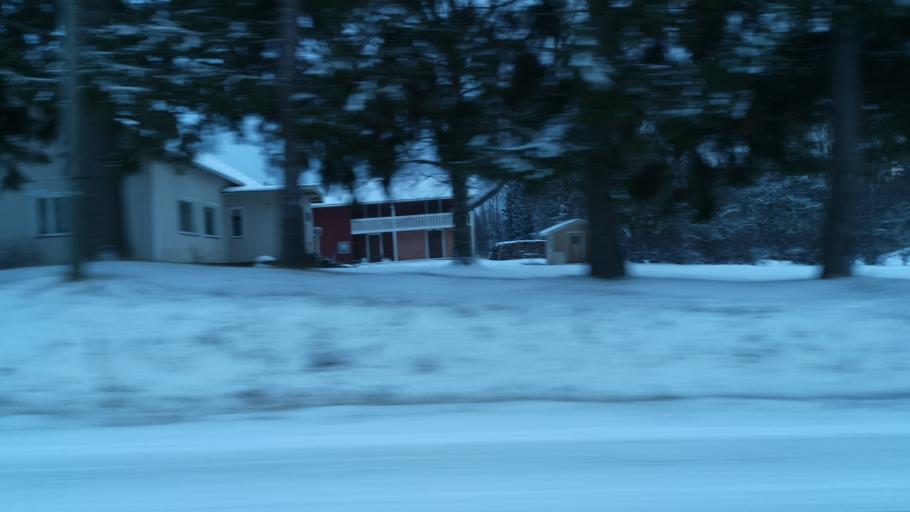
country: FI
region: Southern Savonia
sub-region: Savonlinna
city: Enonkoski
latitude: 62.0624
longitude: 28.7297
